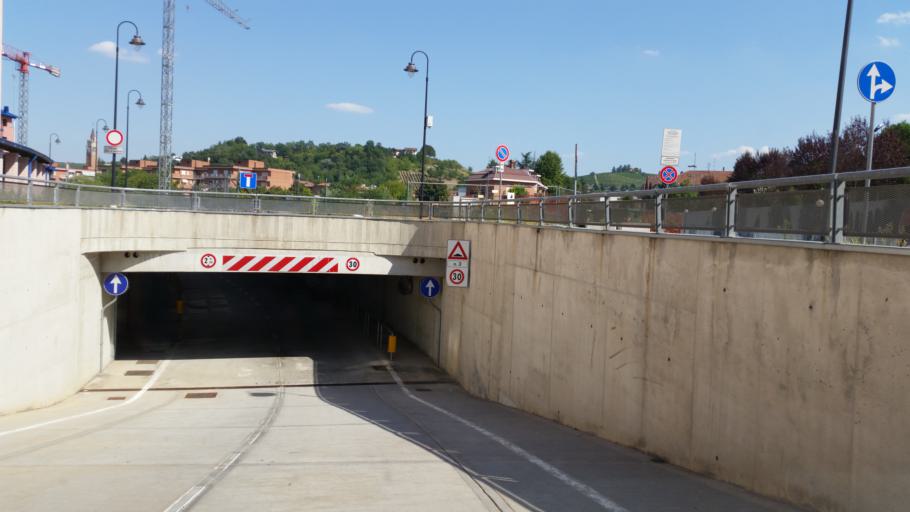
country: IT
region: Piedmont
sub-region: Provincia di Cuneo
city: Alba
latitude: 44.6914
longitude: 8.0155
